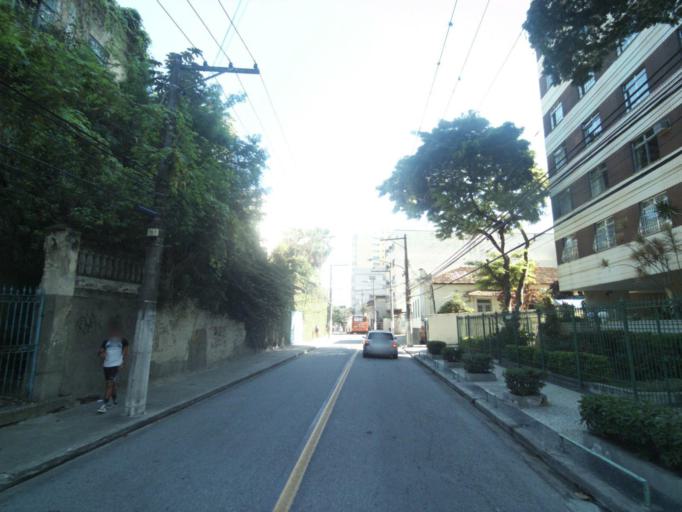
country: BR
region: Rio de Janeiro
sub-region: Niteroi
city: Niteroi
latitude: -22.9035
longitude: -43.1302
